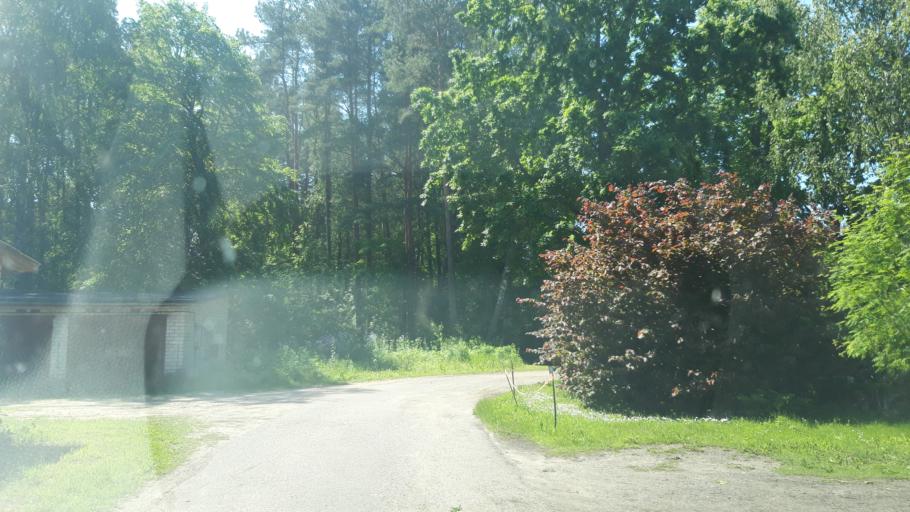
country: LV
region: Saulkrastu
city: Saulkrasti
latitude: 57.2546
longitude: 24.4186
